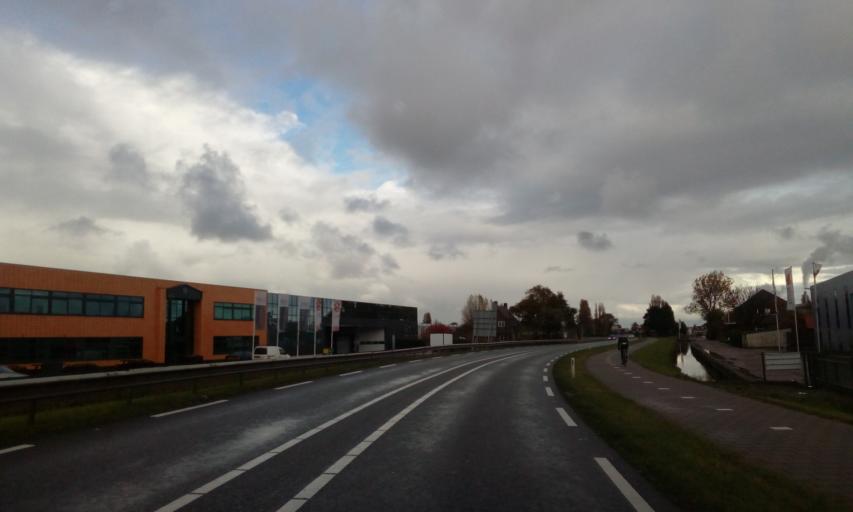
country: NL
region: South Holland
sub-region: Gemeente Westland
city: Honselersdijk
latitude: 52.0075
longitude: 4.2124
